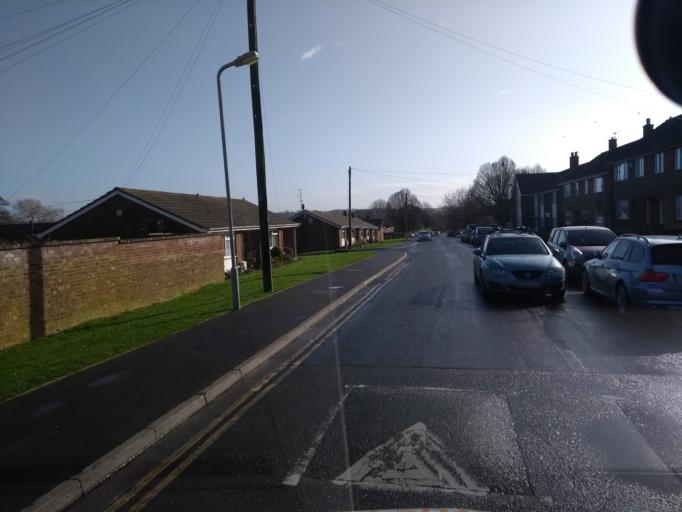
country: GB
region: England
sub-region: Somerset
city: Yeovil
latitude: 50.9534
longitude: -2.6156
